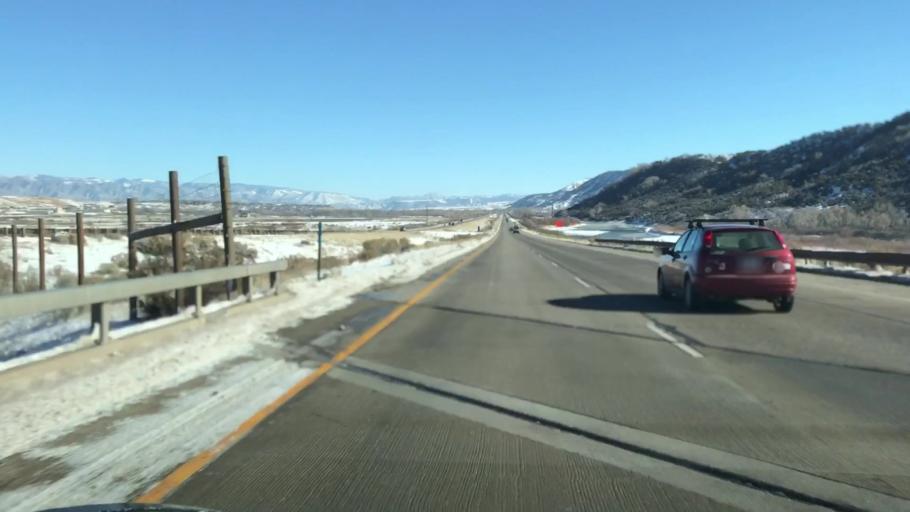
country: US
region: Colorado
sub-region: Garfield County
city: Rifle
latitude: 39.5200
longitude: -107.8371
